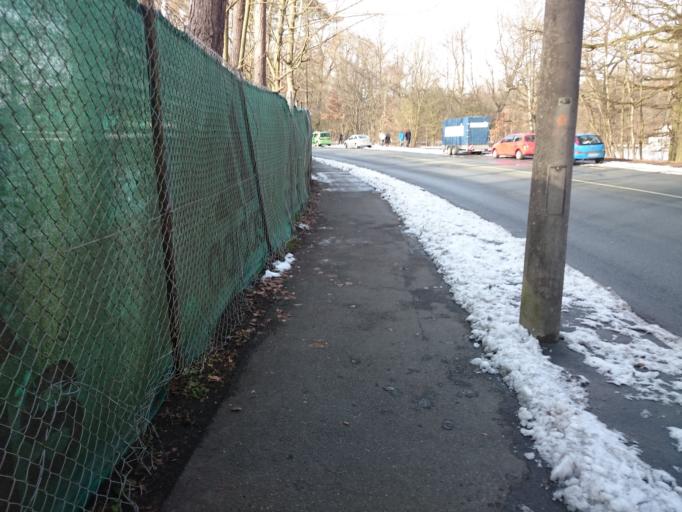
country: DE
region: Bavaria
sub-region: Regierungsbezirk Mittelfranken
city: Nuernberg
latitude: 49.4369
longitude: 11.1341
